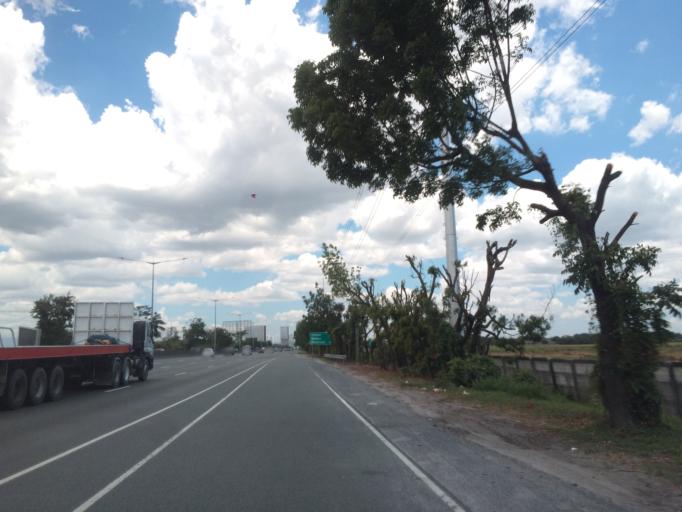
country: PH
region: Central Luzon
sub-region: Province of Bulacan
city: Bocaue
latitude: 14.8210
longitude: 120.9247
